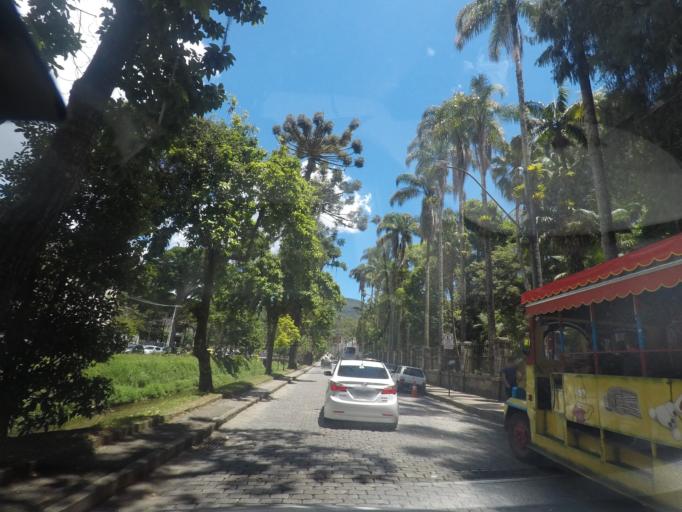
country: BR
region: Rio de Janeiro
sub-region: Petropolis
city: Petropolis
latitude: -22.5086
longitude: -43.1762
